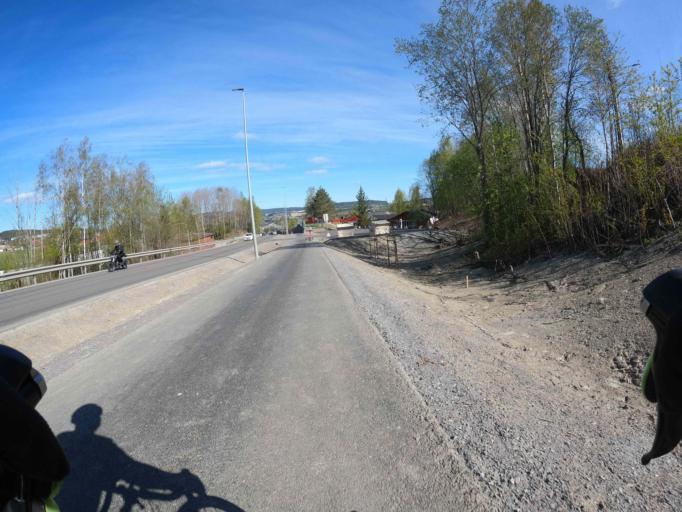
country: NO
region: Akershus
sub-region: Lorenskog
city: Kjenn
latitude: 59.9646
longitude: 10.9949
